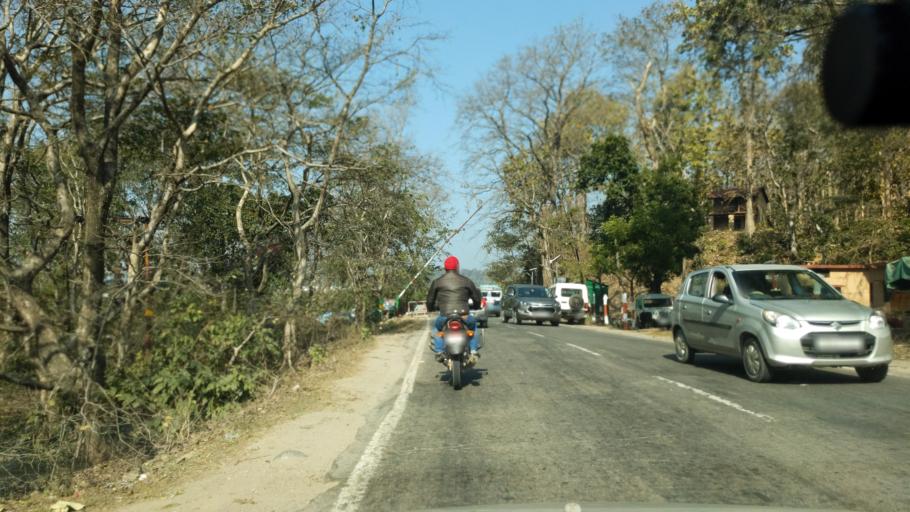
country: IN
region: Uttarakhand
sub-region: Naini Tal
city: Ramnagar
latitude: 29.3858
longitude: 79.1421
